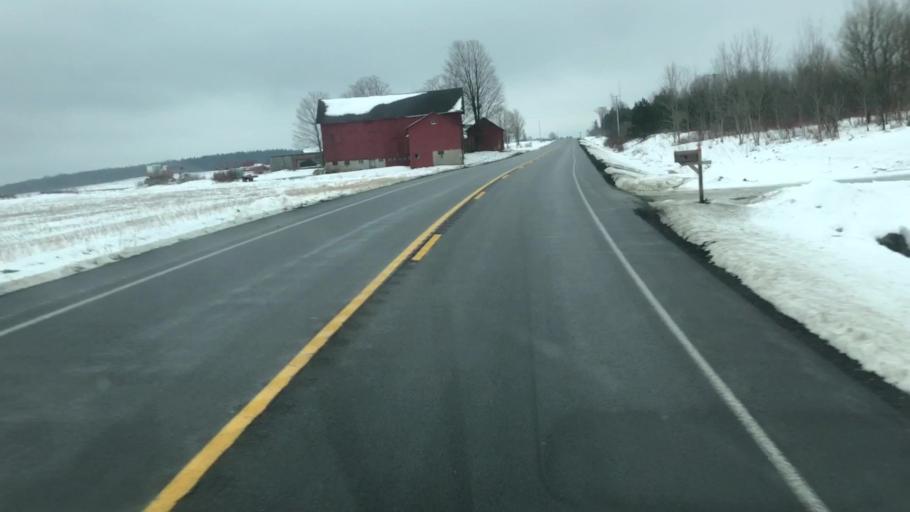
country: US
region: New York
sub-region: Cayuga County
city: Moravia
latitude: 42.7686
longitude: -76.3320
